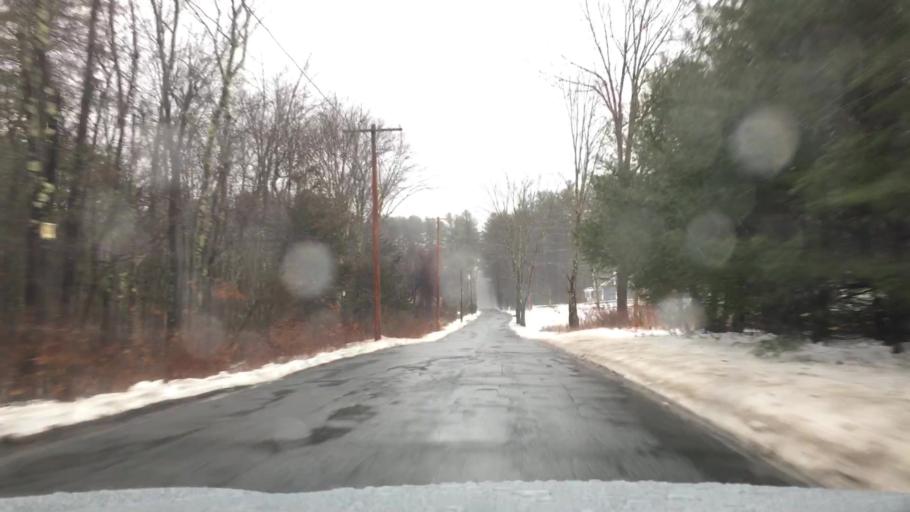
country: US
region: Massachusetts
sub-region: Hampshire County
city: Belchertown
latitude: 42.2676
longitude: -72.4554
